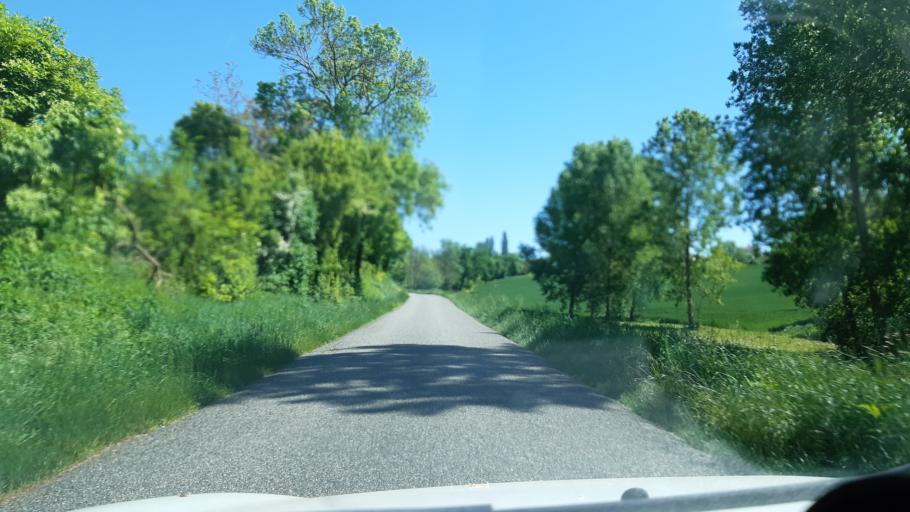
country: FR
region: Midi-Pyrenees
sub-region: Departement du Gers
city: Samatan
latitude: 43.5182
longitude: 0.9935
